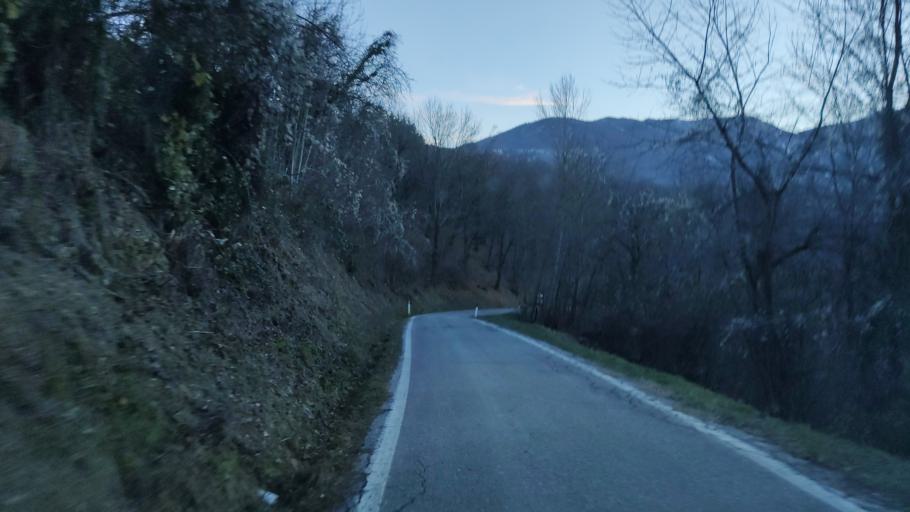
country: IT
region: Piedmont
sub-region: Provincia di Cuneo
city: Lisio
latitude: 44.2933
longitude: 7.9815
